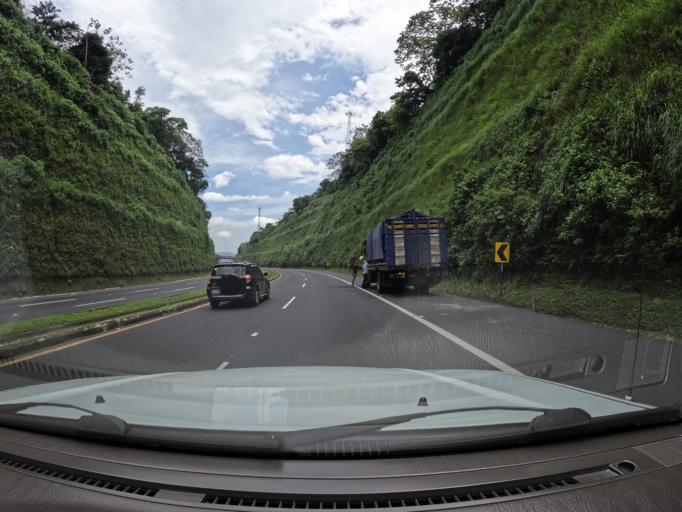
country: GT
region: Escuintla
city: Palin
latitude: 14.3890
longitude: -90.7647
